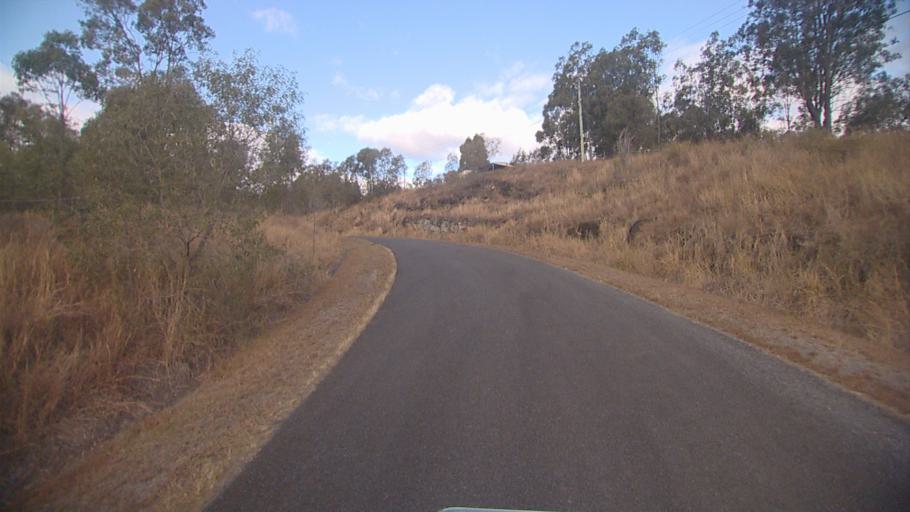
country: AU
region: Queensland
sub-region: Logan
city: Cedar Vale
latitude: -27.9039
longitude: 153.0662
